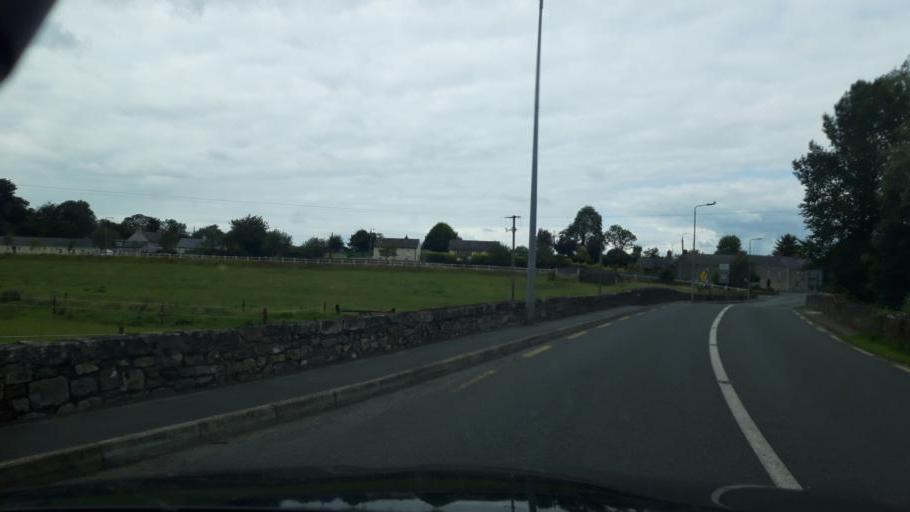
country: IE
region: Leinster
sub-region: Kilkenny
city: Thomastown
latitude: 52.6264
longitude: -7.0726
